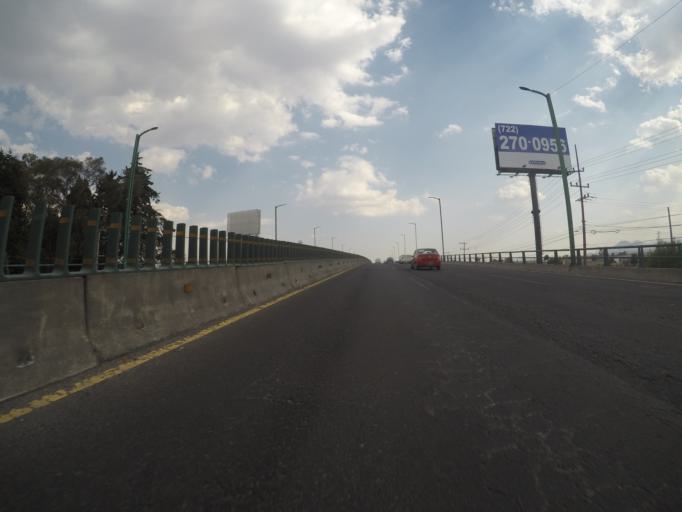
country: MX
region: Morelos
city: San Miguel Totocuitlapilco
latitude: 19.2370
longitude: -99.5985
